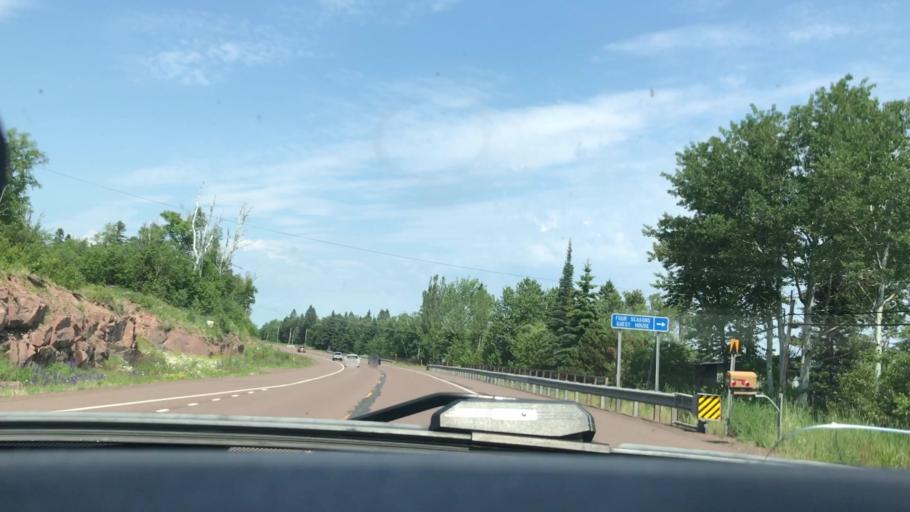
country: US
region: Minnesota
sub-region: Cook County
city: Grand Marais
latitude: 47.6094
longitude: -90.7676
